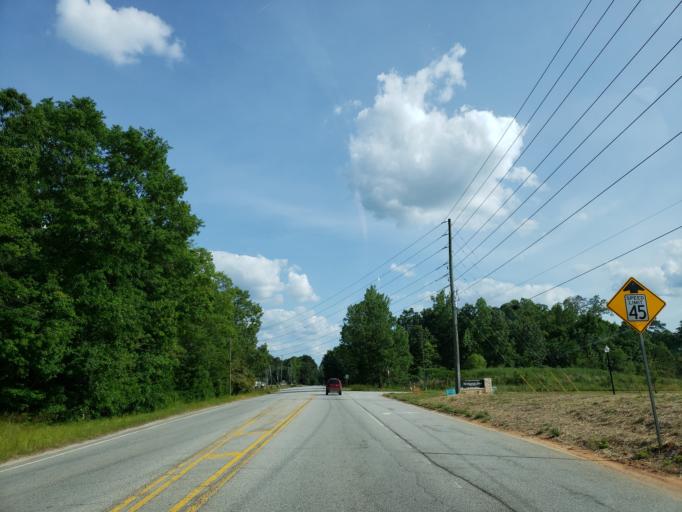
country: US
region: Georgia
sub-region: Carroll County
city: Carrollton
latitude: 33.6075
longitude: -85.0802
